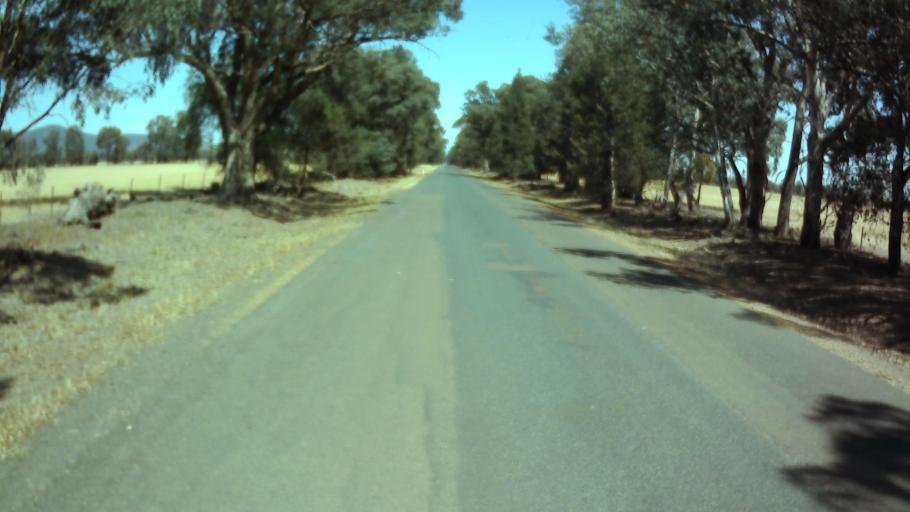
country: AU
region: New South Wales
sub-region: Weddin
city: Grenfell
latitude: -33.8671
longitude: 148.0615
